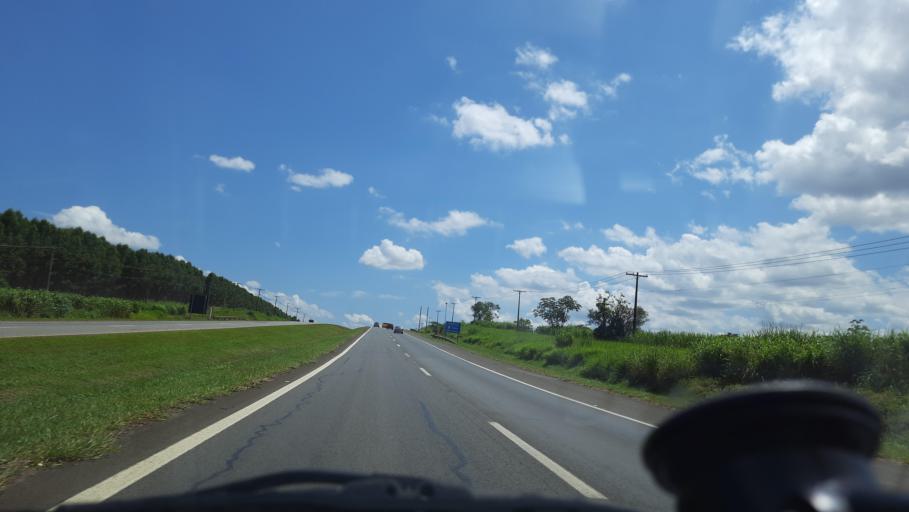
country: BR
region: Sao Paulo
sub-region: Moji-Guacu
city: Mogi-Gaucu
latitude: -22.3345
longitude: -46.9592
